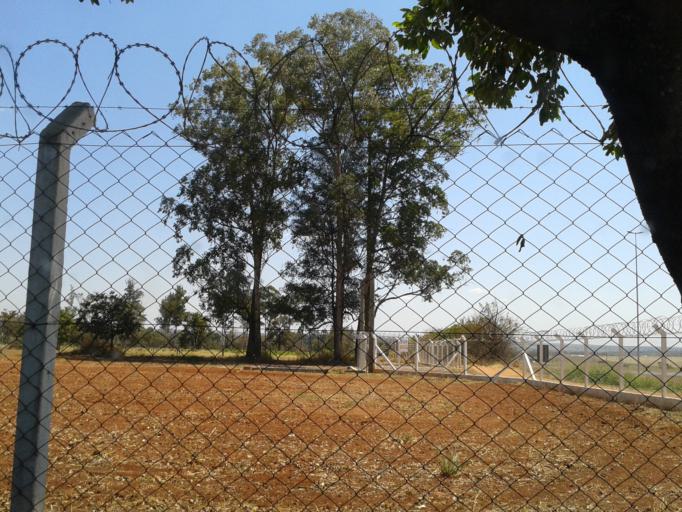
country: BR
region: Minas Gerais
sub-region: Uberlandia
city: Uberlandia
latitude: -18.8928
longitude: -48.4199
